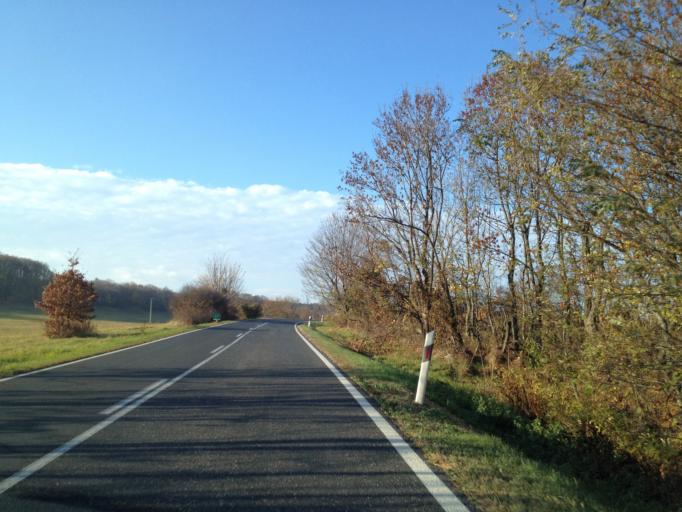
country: HU
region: Veszprem
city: Zirc
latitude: 47.3110
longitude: 17.8841
